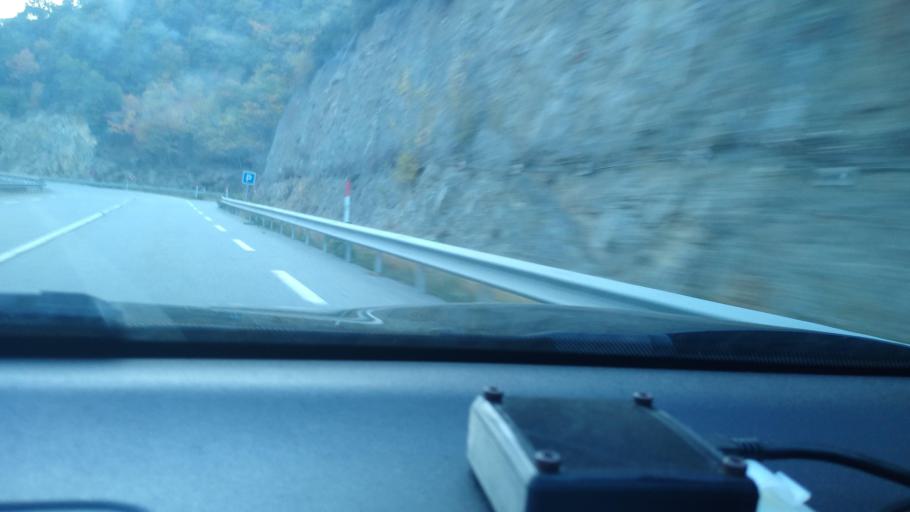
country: FR
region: Languedoc-Roussillon
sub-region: Departement des Pyrenees-Orientales
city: Vernet-les-Bains
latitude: 42.5211
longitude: 2.2074
